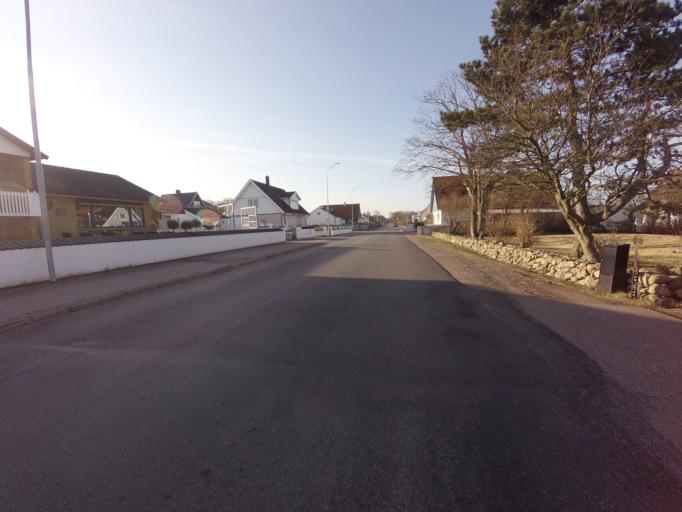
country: SE
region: Skane
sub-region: Hoganas Kommun
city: Hoganas
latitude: 56.1889
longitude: 12.5571
